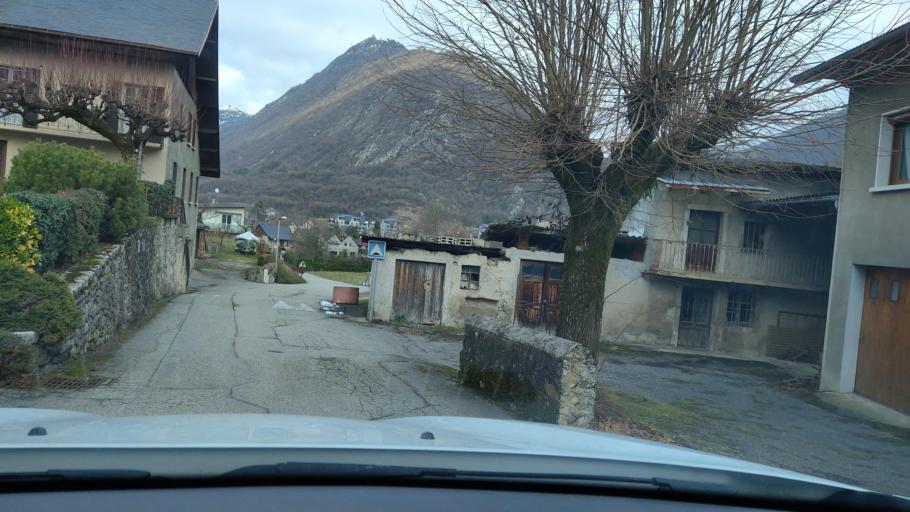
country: FR
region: Rhone-Alpes
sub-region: Departement de la Savoie
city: Challes-les-Eaux
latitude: 45.5343
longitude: 5.9905
